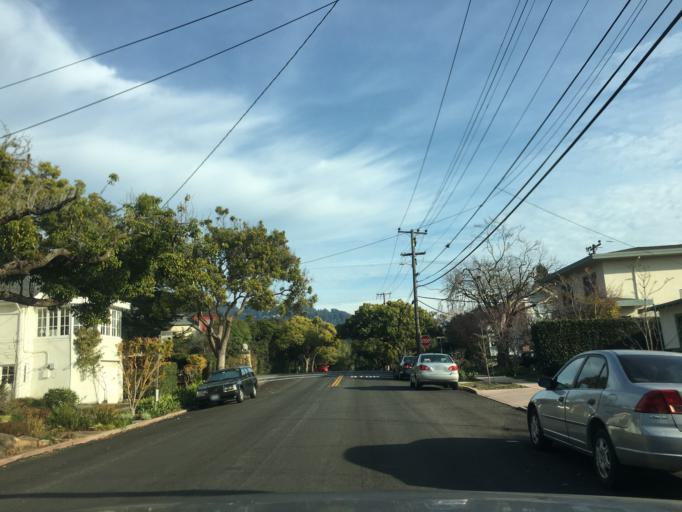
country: US
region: California
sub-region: Alameda County
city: Berkeley
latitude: 37.8859
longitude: -122.2788
